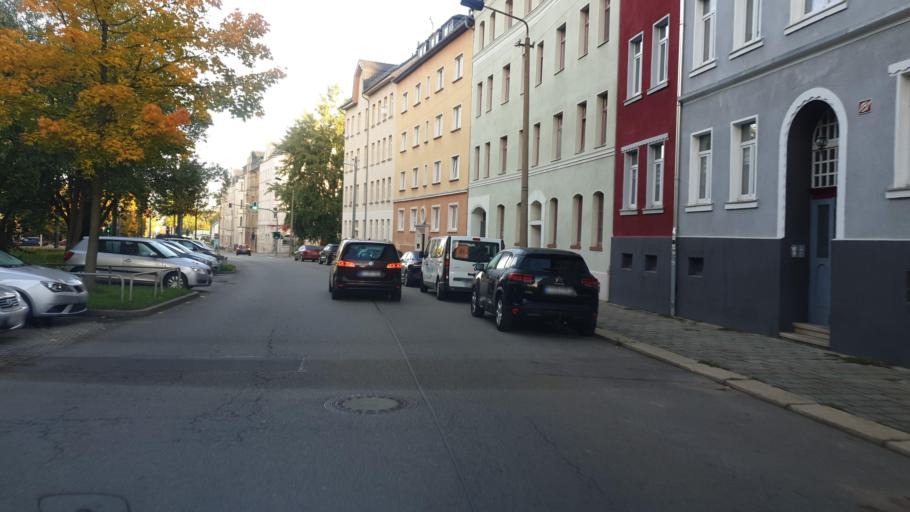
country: DE
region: Saxony
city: Chemnitz
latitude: 50.8129
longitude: 12.9489
